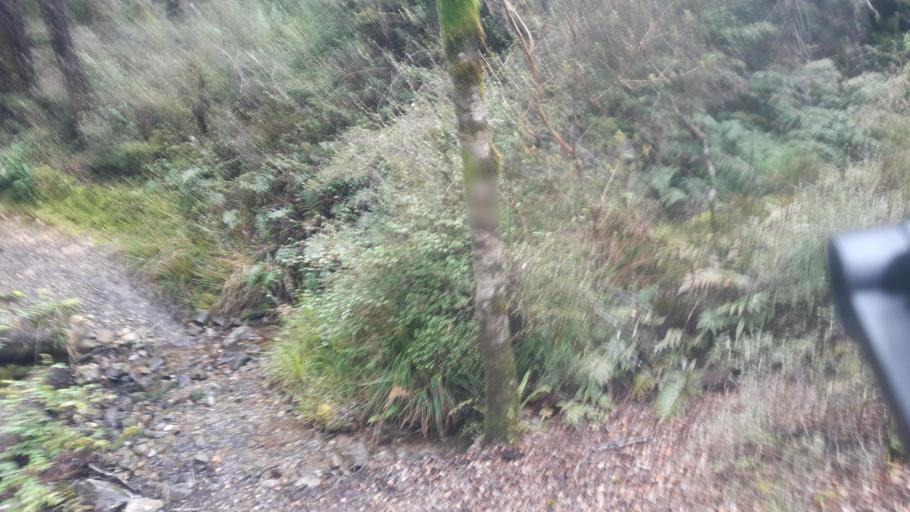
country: NZ
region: Tasman
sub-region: Tasman District
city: Wakefield
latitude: -41.7744
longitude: 172.8079
